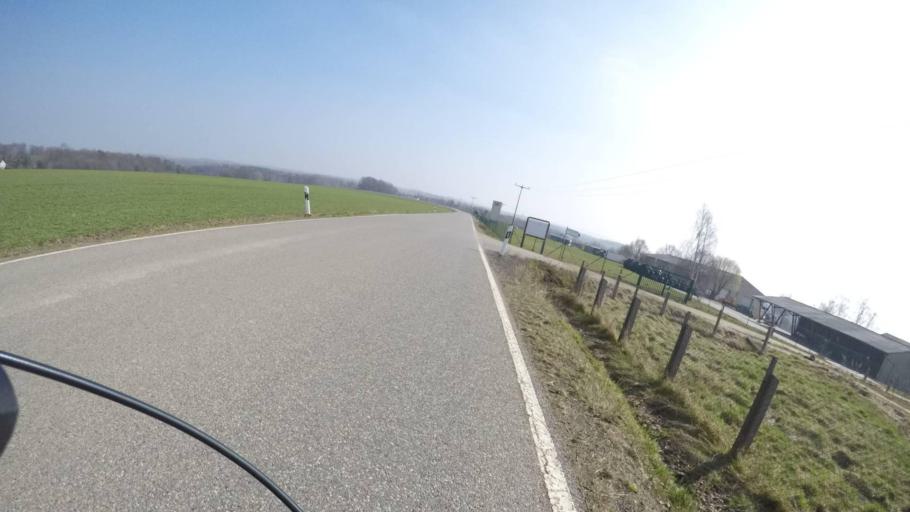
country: DE
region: Thuringia
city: Juckelberg
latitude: 50.9101
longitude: 12.6612
